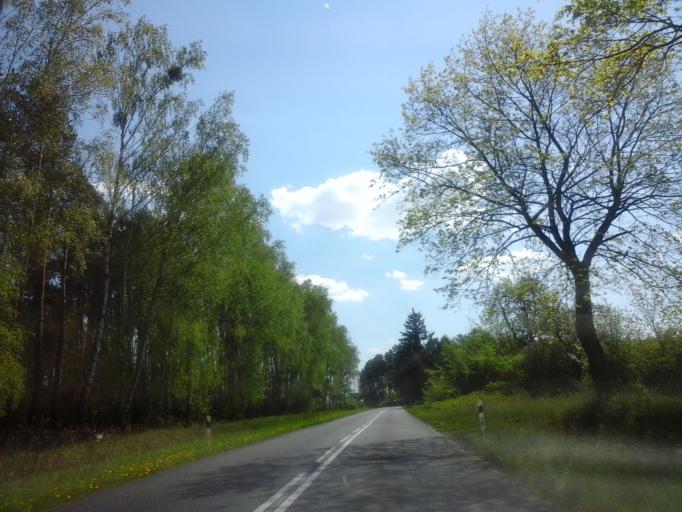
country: PL
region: Lubusz
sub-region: Powiat strzelecko-drezdenecki
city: Dobiegniew
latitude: 52.9950
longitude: 15.7482
